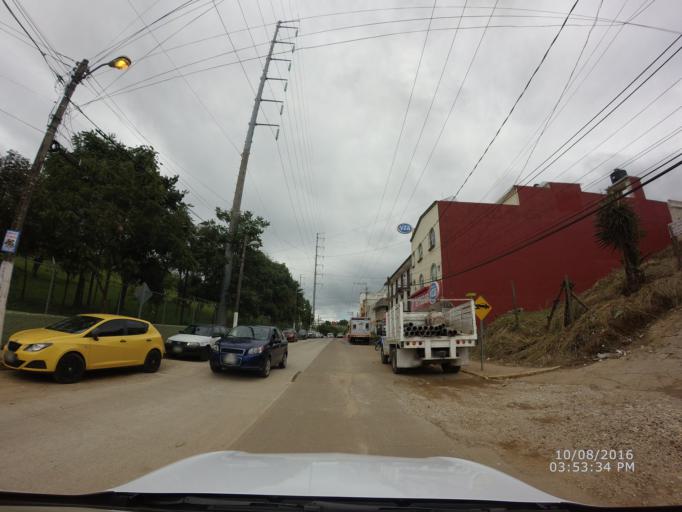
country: MX
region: Veracruz
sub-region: Xalapa
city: Colonia Santa Barbara
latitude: 19.5015
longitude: -96.8789
